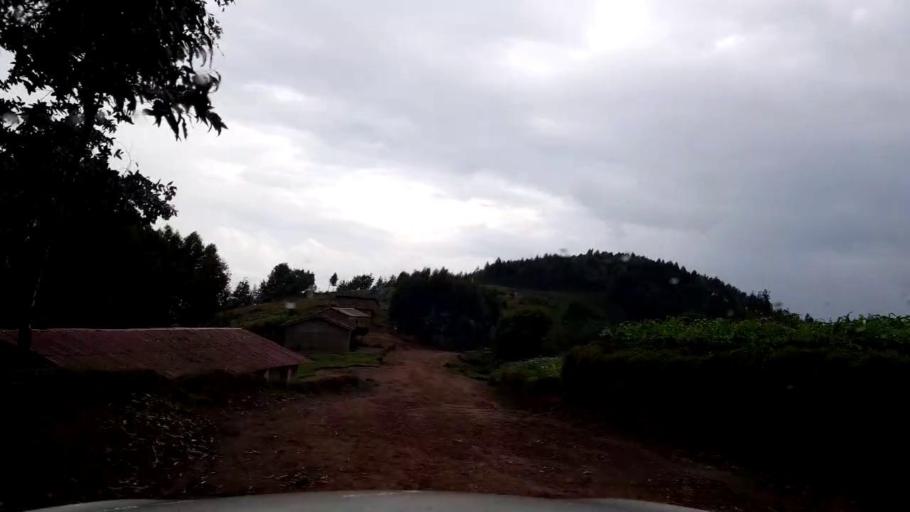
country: RW
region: Western Province
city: Kibuye
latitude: -2.0178
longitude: 29.4652
